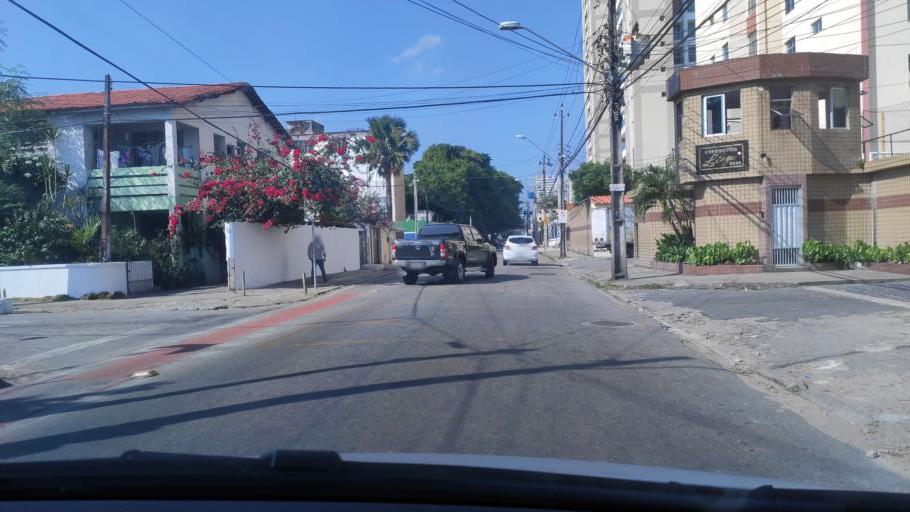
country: BR
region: Ceara
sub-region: Fortaleza
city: Fortaleza
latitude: -3.7403
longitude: -38.5337
